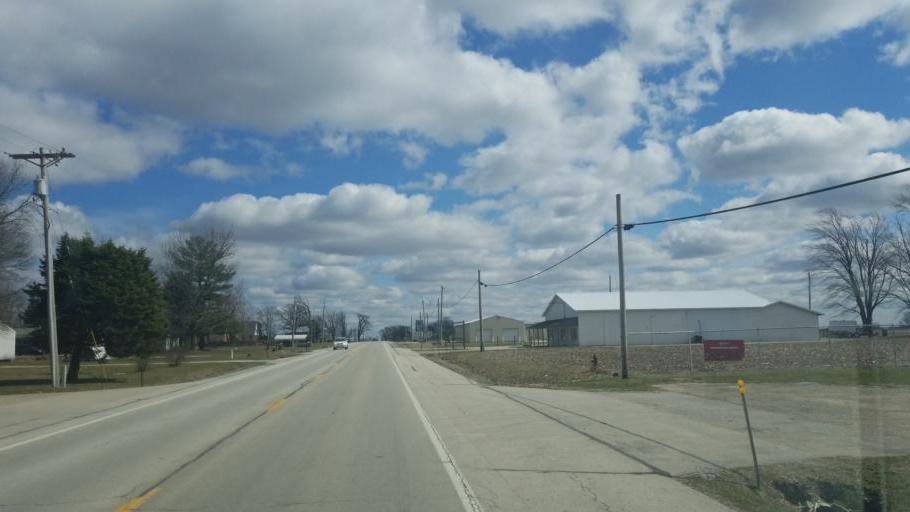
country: US
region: Illinois
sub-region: Douglas County
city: Atwood
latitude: 39.7918
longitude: -88.4598
